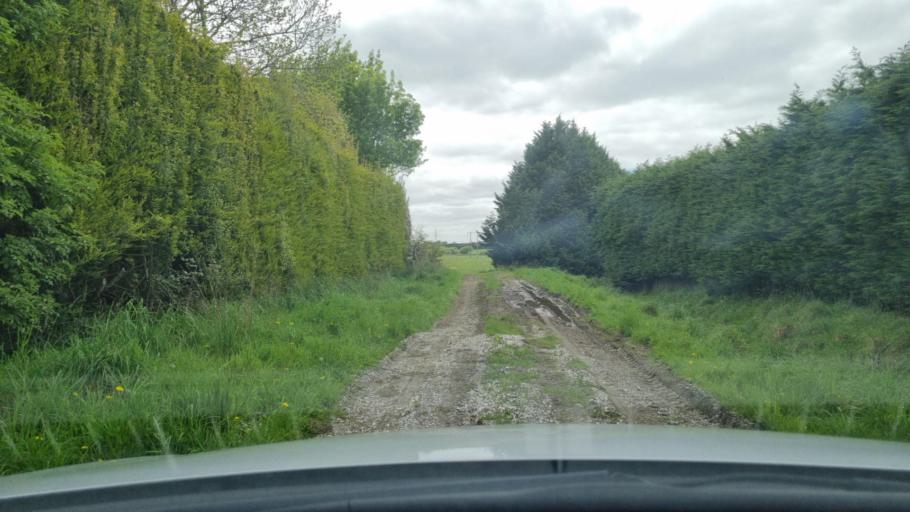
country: NZ
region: Southland
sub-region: Invercargill City
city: Invercargill
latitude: -46.3890
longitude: 168.4041
